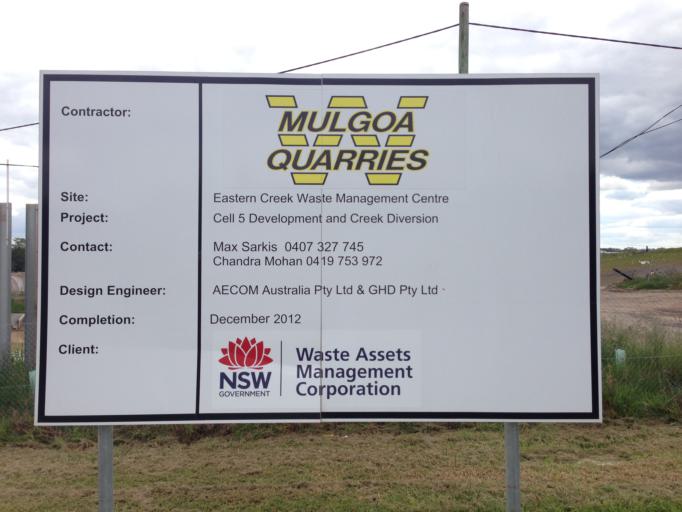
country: AU
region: New South Wales
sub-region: Fairfield
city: Horsley Park
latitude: -33.8128
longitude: 150.8658
